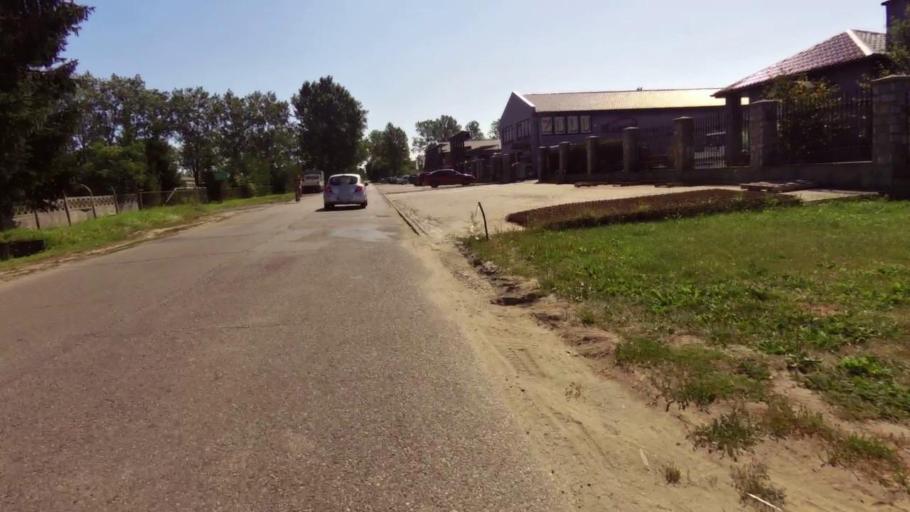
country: PL
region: West Pomeranian Voivodeship
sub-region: Powiat drawski
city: Zlocieniec
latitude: 53.5259
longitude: 16.0195
